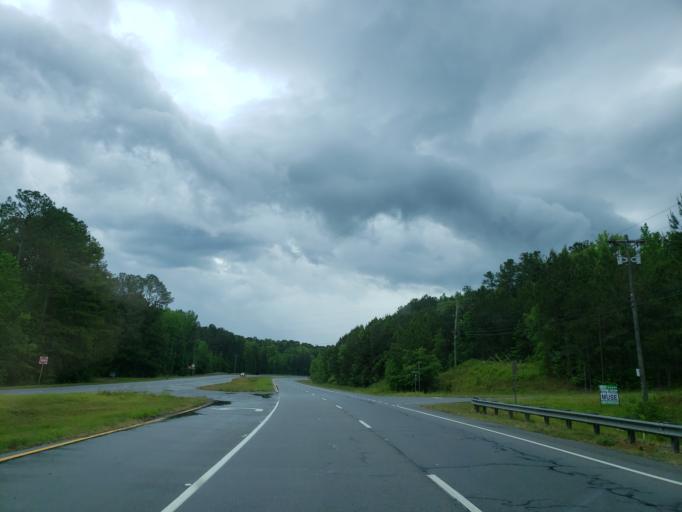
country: US
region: Georgia
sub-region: Haralson County
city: Buchanan
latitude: 33.8608
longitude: -85.2121
